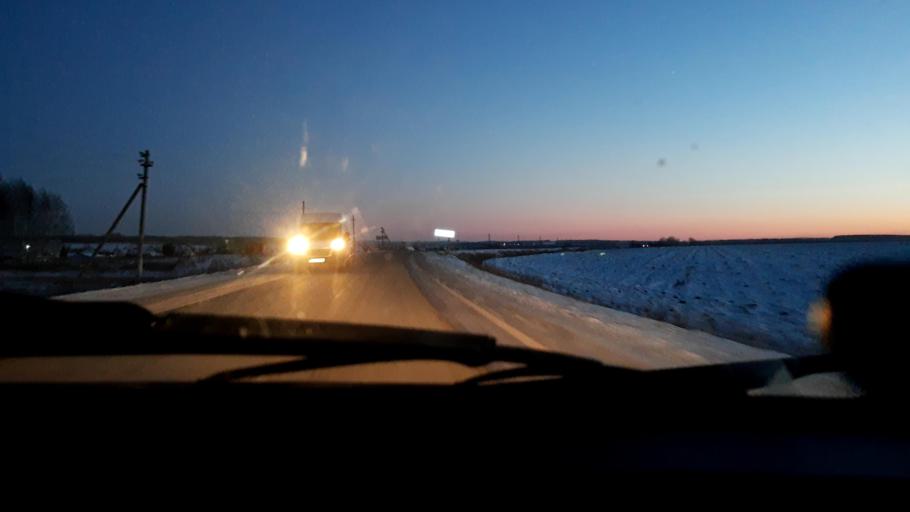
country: RU
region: Bashkortostan
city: Iglino
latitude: 54.7542
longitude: 56.3995
